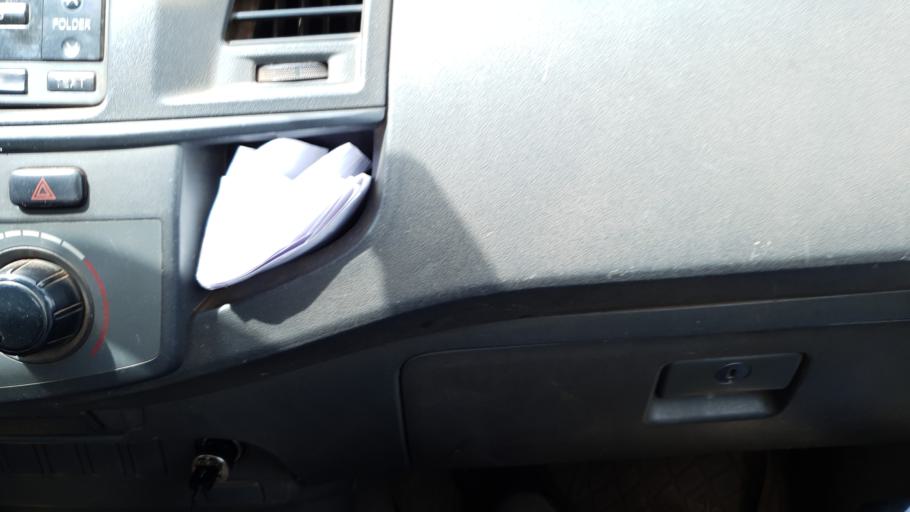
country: ML
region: Koulikoro
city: Kolokani
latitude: 13.4310
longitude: -8.2374
